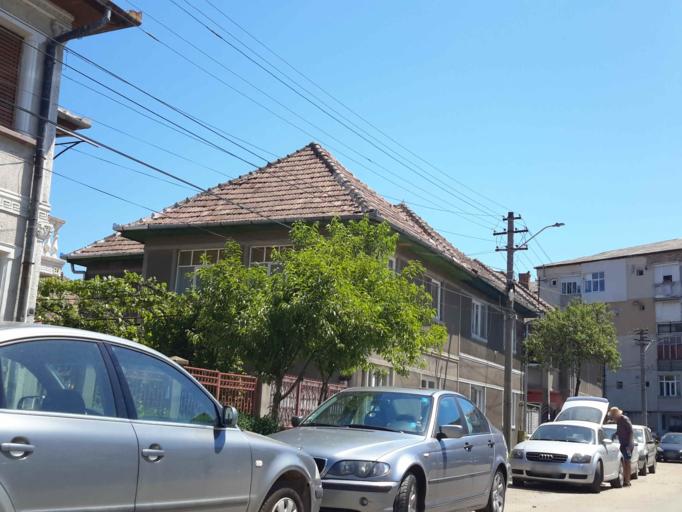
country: RO
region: Alba
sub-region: Municipiul Blaj
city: Veza
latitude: 46.1753
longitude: 23.9286
